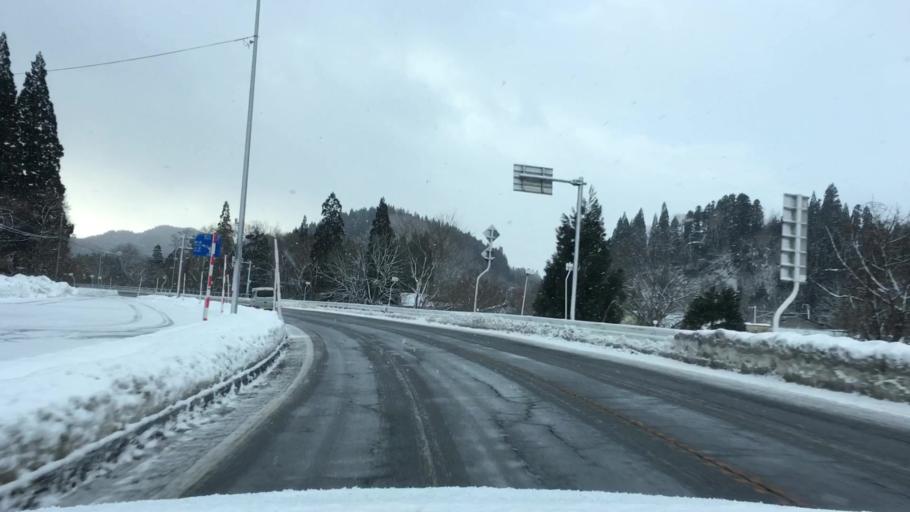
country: JP
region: Akita
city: Odate
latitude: 40.4459
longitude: 140.6341
